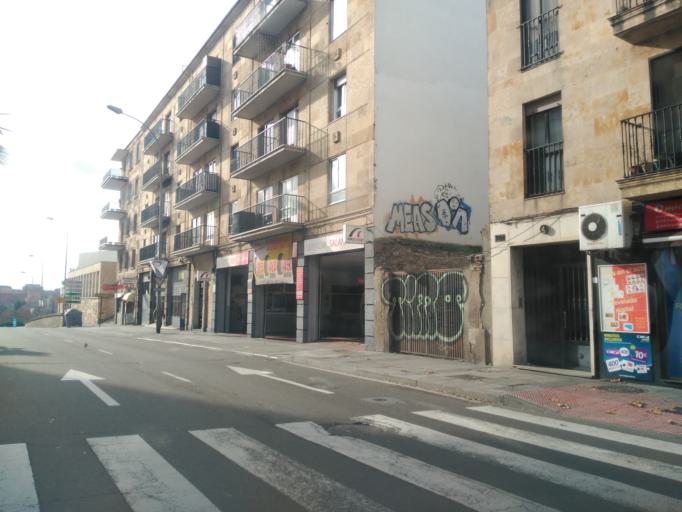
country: ES
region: Castille and Leon
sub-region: Provincia de Salamanca
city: Salamanca
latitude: 40.9598
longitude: -5.6599
